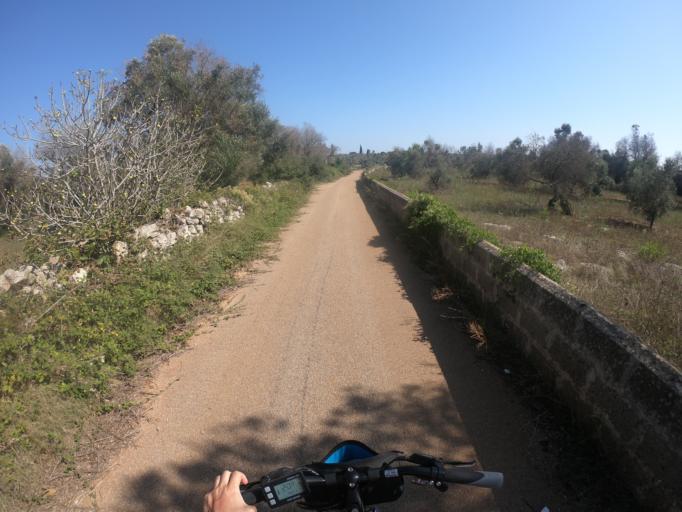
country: IT
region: Apulia
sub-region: Provincia di Lecce
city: Specchia
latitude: 39.9200
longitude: 18.2845
